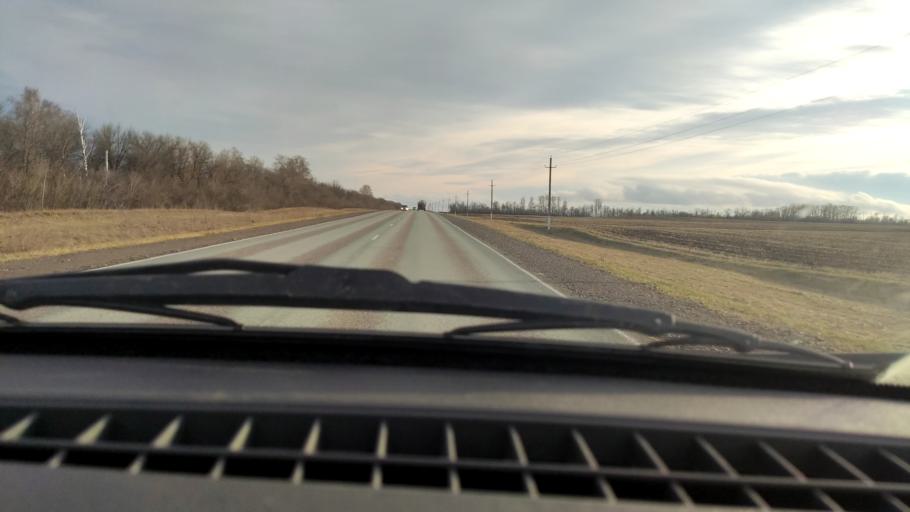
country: RU
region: Bashkortostan
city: Davlekanovo
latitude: 54.3227
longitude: 55.1579
